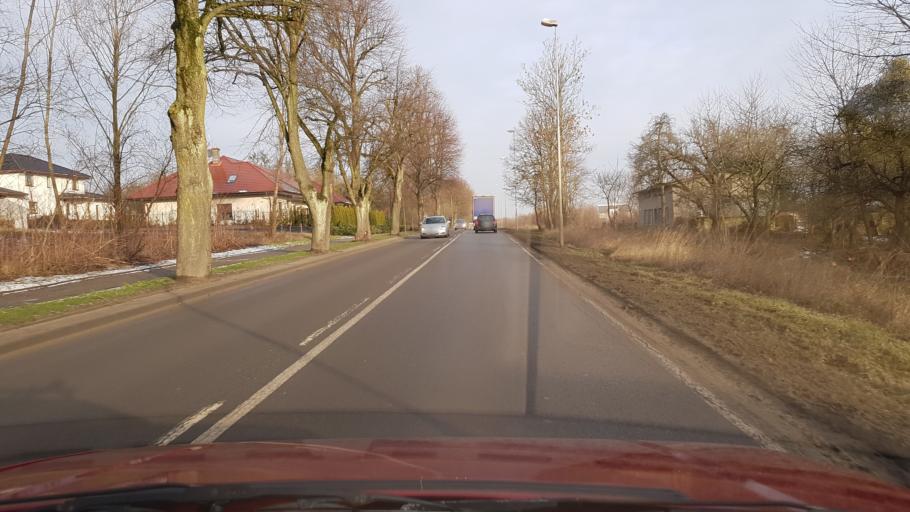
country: PL
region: West Pomeranian Voivodeship
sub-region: Szczecin
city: Szczecin
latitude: 53.4843
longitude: 14.5864
